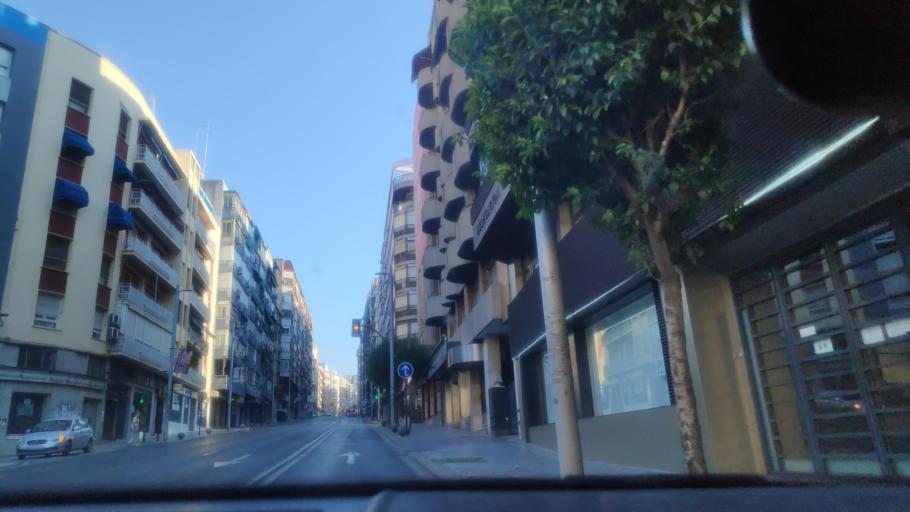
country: ES
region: Andalusia
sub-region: Provincia de Jaen
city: Jaen
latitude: 37.7712
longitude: -3.7864
